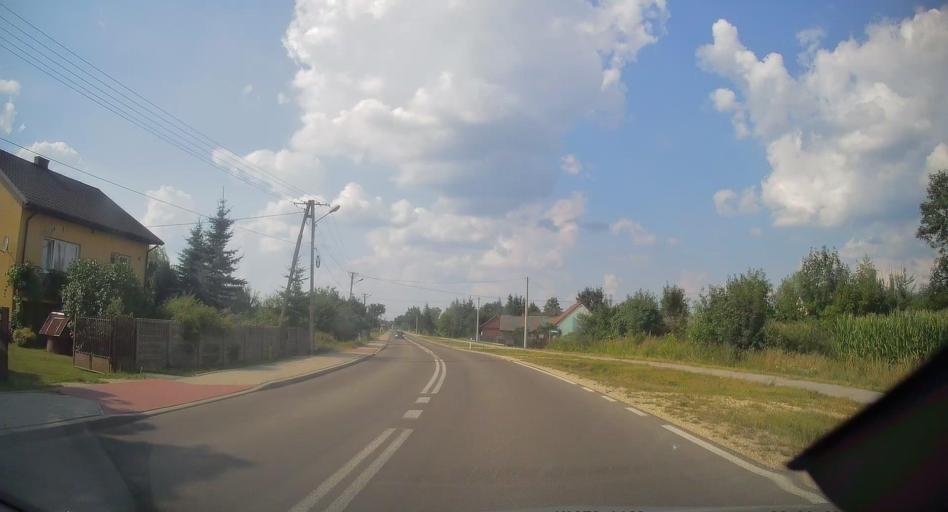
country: PL
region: Swietokrzyskie
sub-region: Powiat konecki
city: Radoszyce
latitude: 51.0461
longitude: 20.2837
